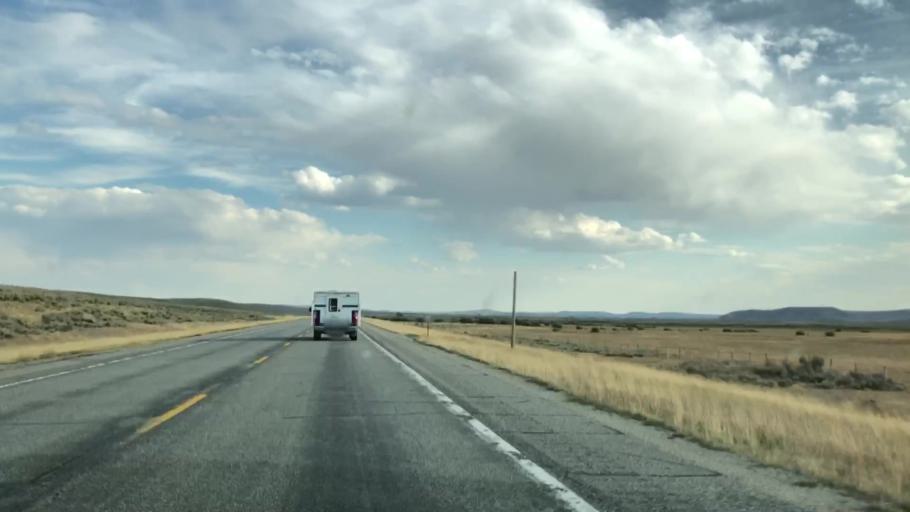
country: US
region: Wyoming
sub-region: Sublette County
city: Pinedale
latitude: 43.0290
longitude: -110.1264
